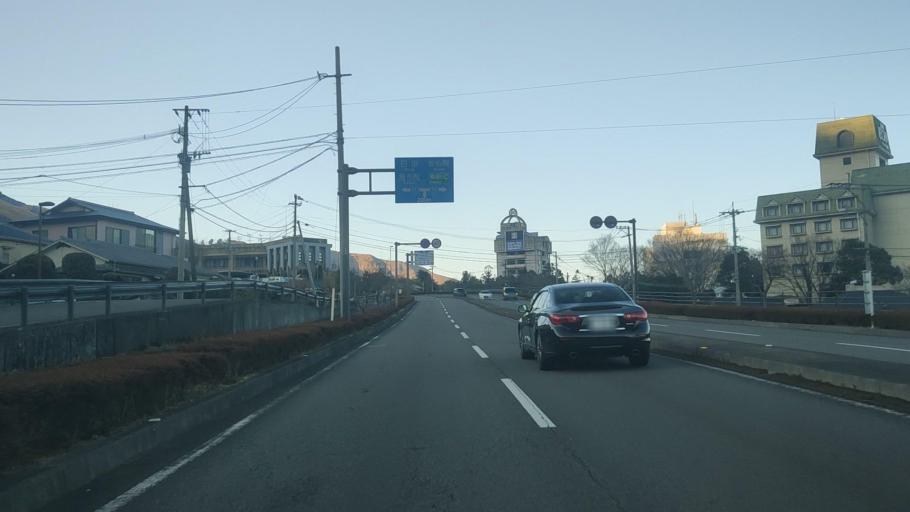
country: JP
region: Oita
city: Beppu
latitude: 33.2891
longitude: 131.4611
